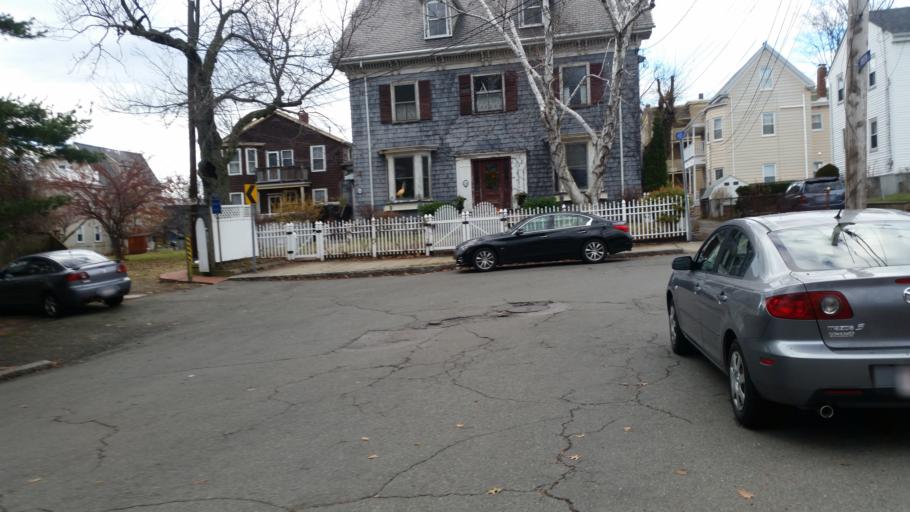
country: US
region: Massachusetts
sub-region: Middlesex County
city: Somerville
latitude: 42.3851
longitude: -71.1090
